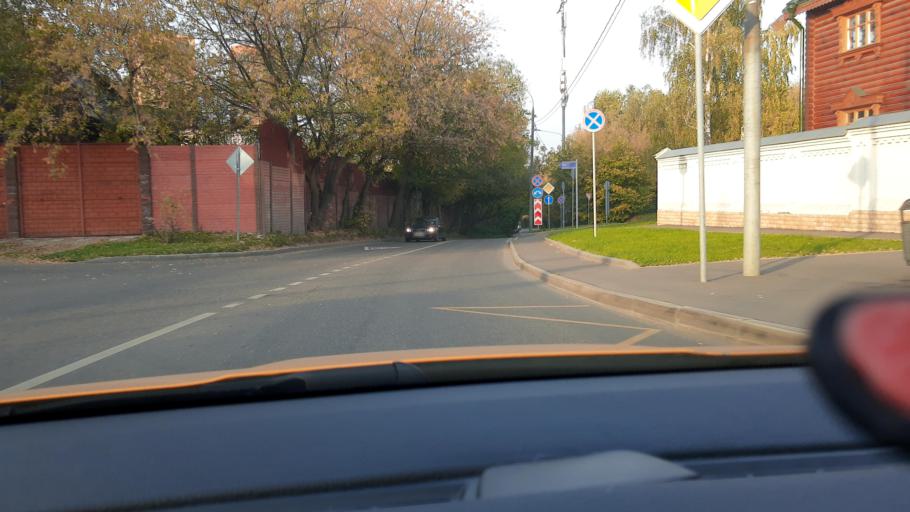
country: RU
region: Moscow
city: Strogino
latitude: 55.7907
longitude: 37.4041
